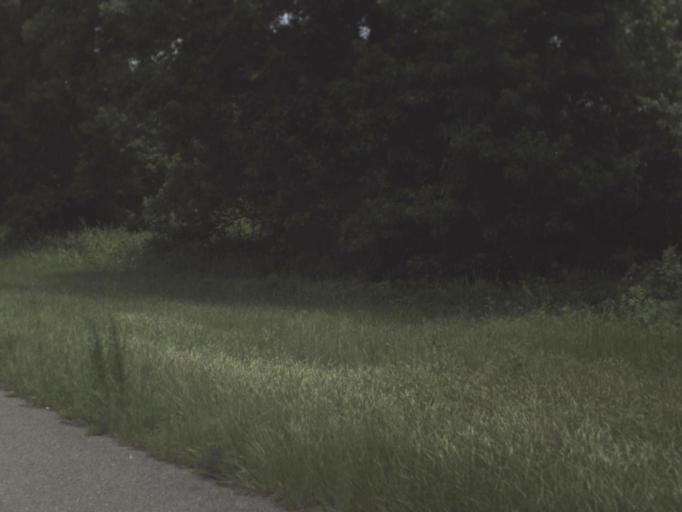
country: US
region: Florida
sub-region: Madison County
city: Madison
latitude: 30.4764
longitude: -83.5584
